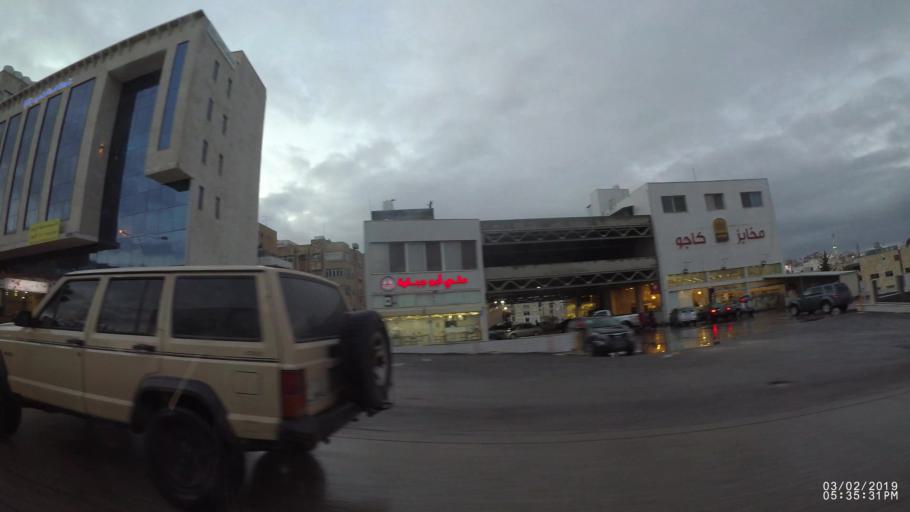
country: JO
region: Amman
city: Al Jubayhah
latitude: 31.9801
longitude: 35.8913
